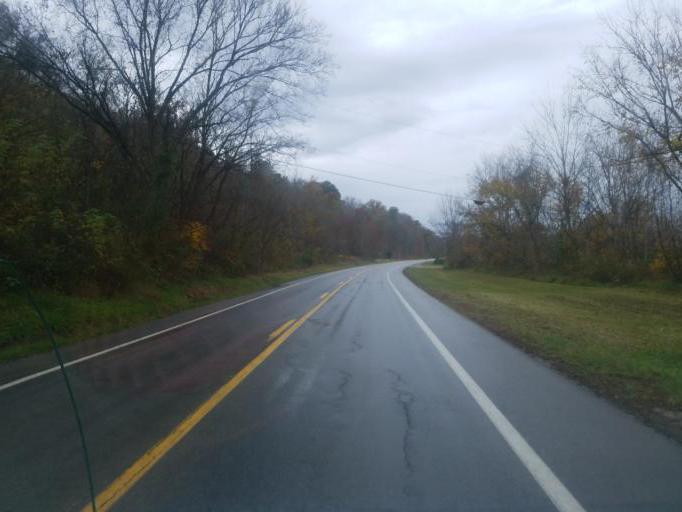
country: US
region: West Virginia
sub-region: Wood County
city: Boaz
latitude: 39.3589
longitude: -81.5050
